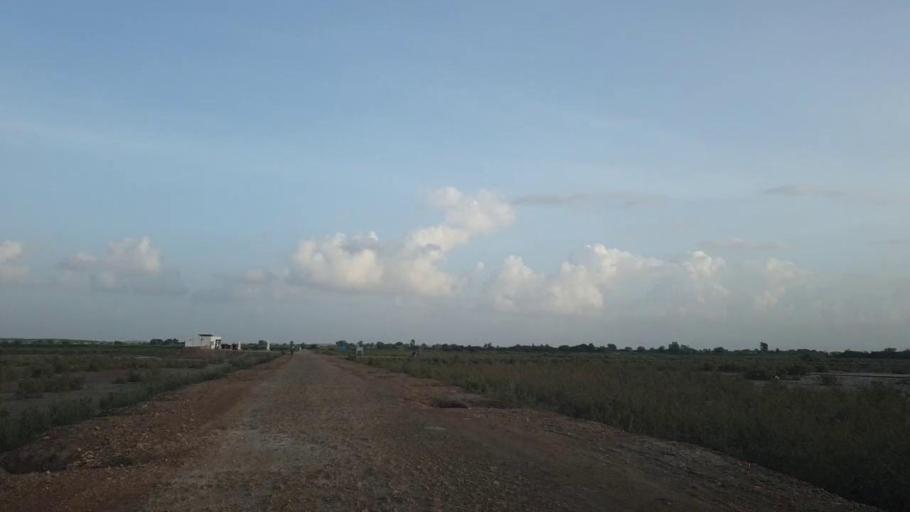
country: PK
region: Sindh
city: Kadhan
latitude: 24.5509
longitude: 69.1240
